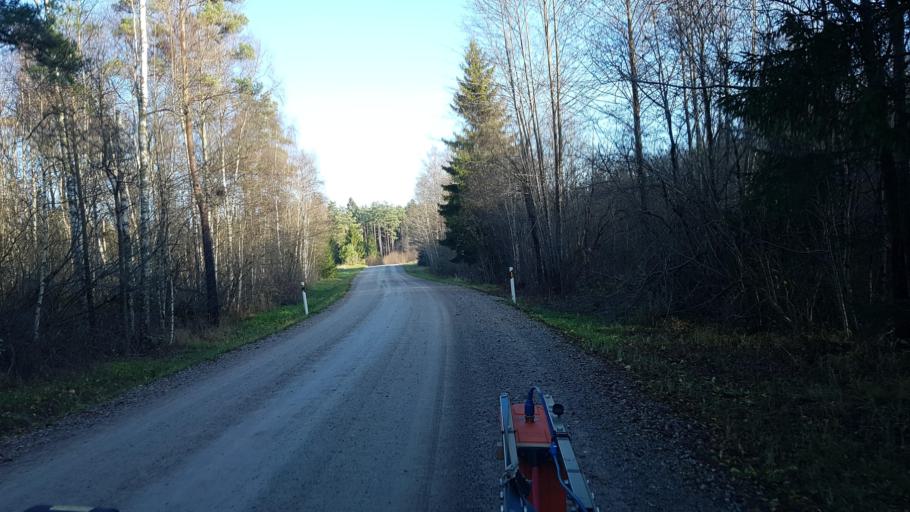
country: EE
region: Harju
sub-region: Nissi vald
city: Turba
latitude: 59.1821
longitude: 24.1389
